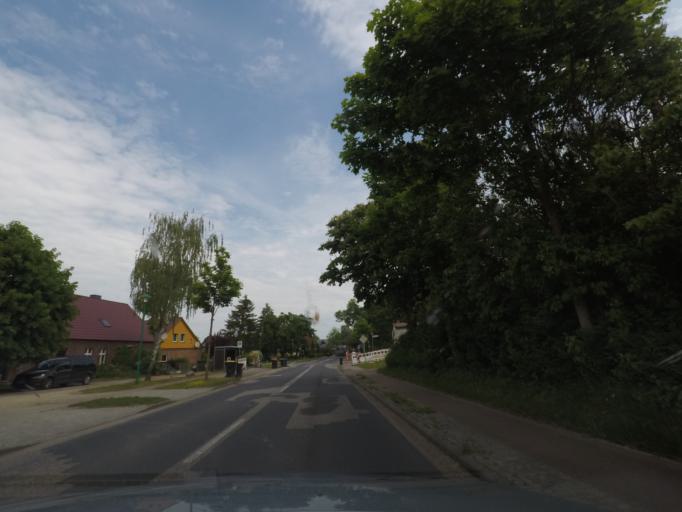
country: DE
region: Brandenburg
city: Schenkenberg
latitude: 53.3454
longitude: 13.9466
